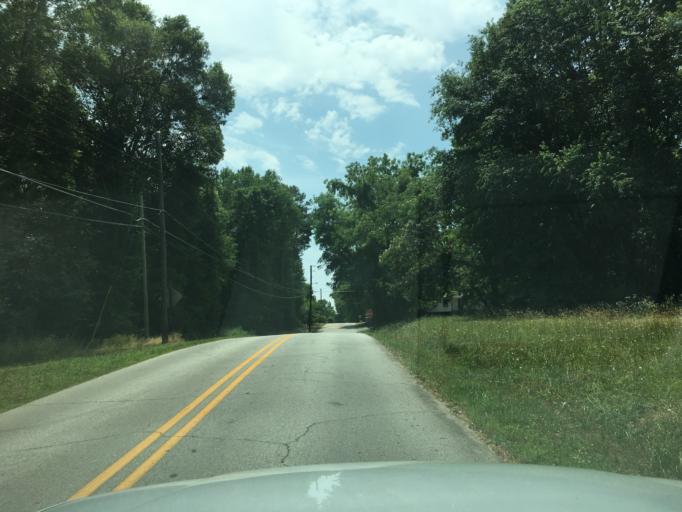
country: US
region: Georgia
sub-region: Hart County
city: Hartwell
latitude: 34.3456
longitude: -82.9346
